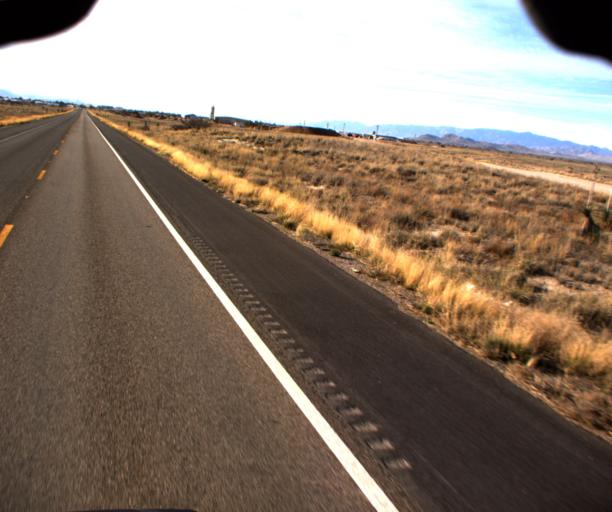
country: US
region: Arizona
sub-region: Cochise County
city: Willcox
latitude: 32.2354
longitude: -109.8070
